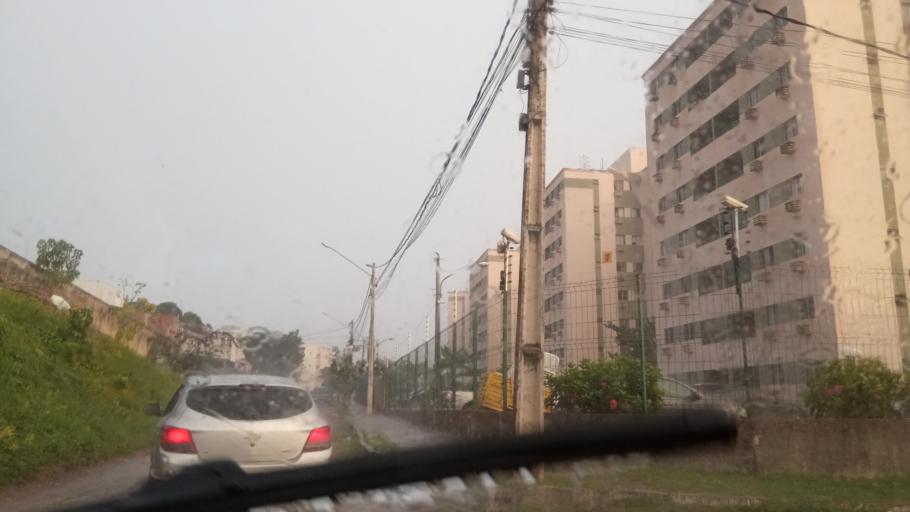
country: BR
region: Pernambuco
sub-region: Jaboatao Dos Guararapes
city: Jaboatao
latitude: -8.2013
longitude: -34.9250
